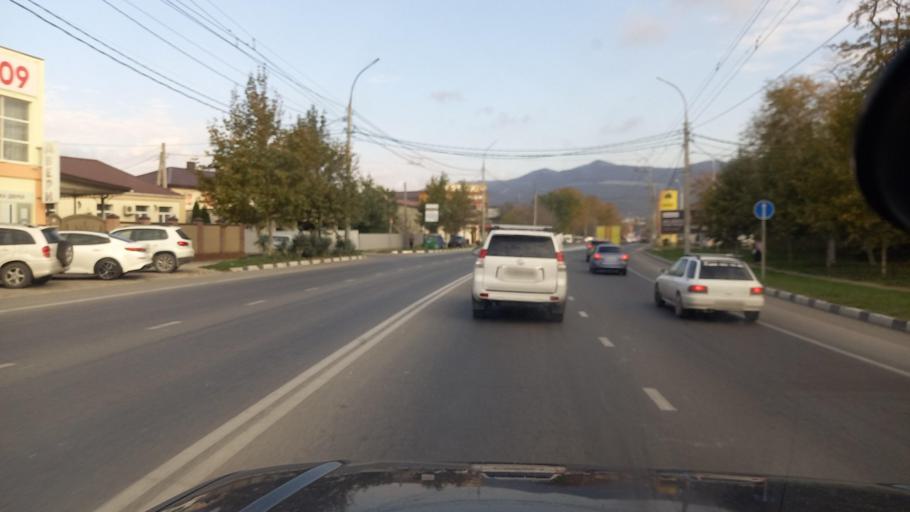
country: RU
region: Krasnodarskiy
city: Gayduk
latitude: 44.7463
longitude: 37.7256
